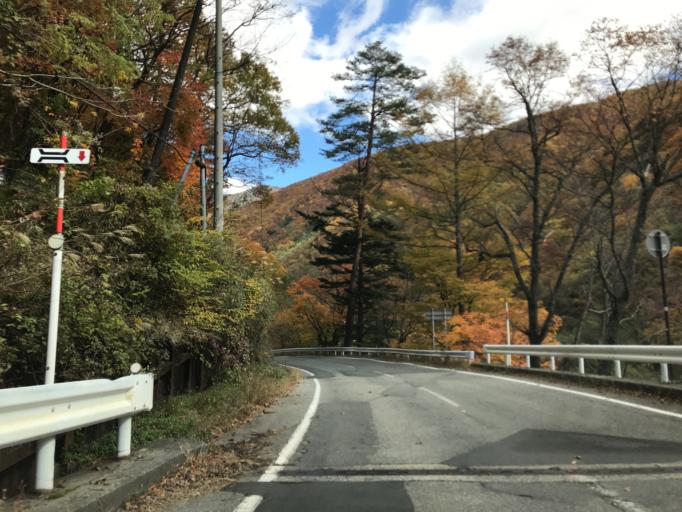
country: JP
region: Nagano
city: Toyoshina
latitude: 36.1306
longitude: 137.6699
